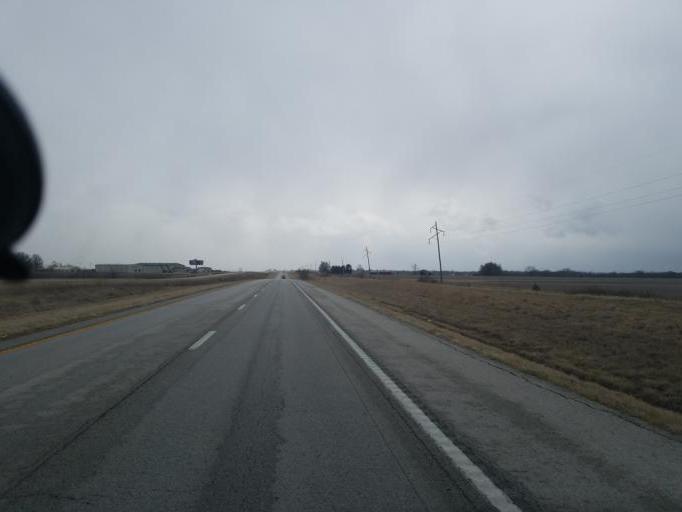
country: US
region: Missouri
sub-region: Randolph County
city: Moberly
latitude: 39.5472
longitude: -92.4530
